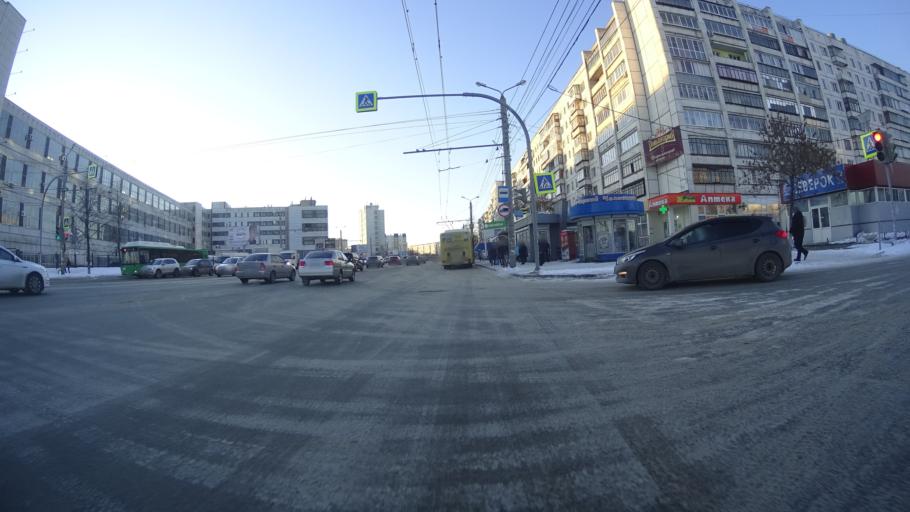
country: RU
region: Chelyabinsk
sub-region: Gorod Chelyabinsk
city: Chelyabinsk
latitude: 55.1925
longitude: 61.3614
